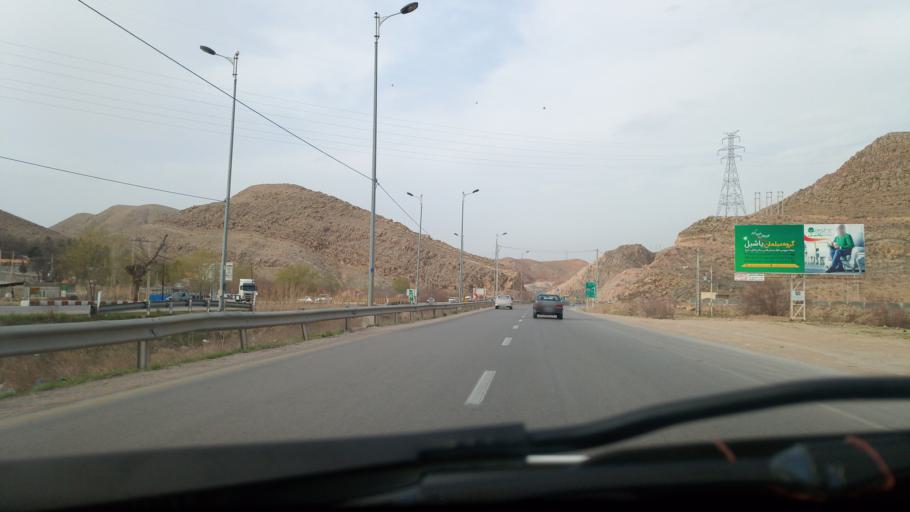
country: IR
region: Khorasan-e Shomali
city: Bojnurd
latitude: 37.4871
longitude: 57.4383
